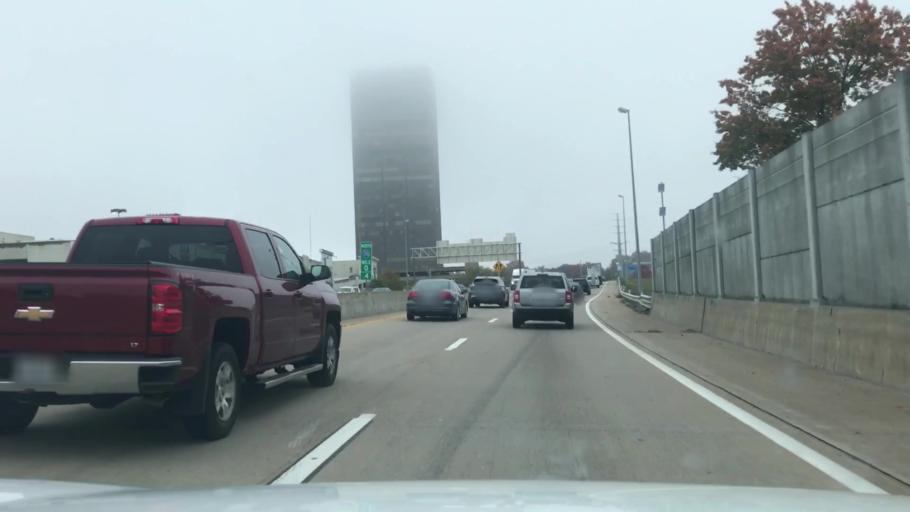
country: US
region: Missouri
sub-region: Saint Louis County
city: Brentwood
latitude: 38.6331
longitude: -90.3441
